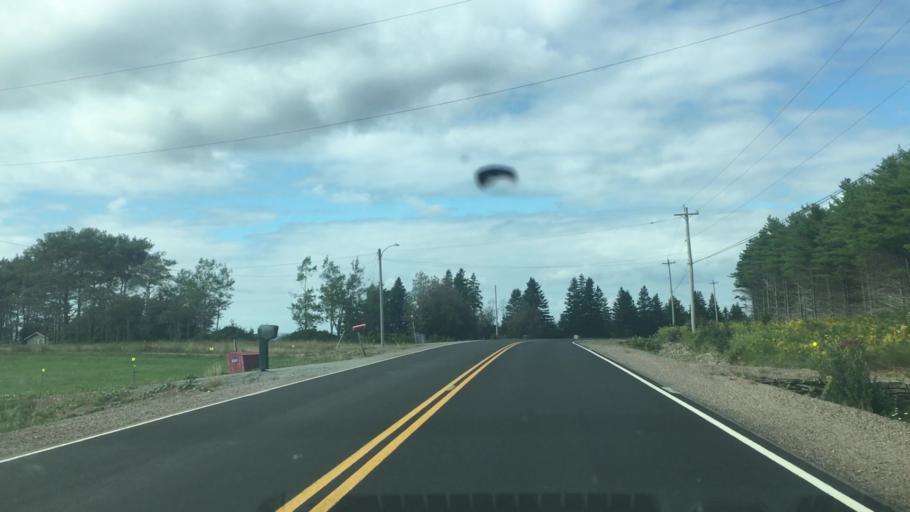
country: CA
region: Nova Scotia
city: Princeville
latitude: 45.7878
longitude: -60.7403
